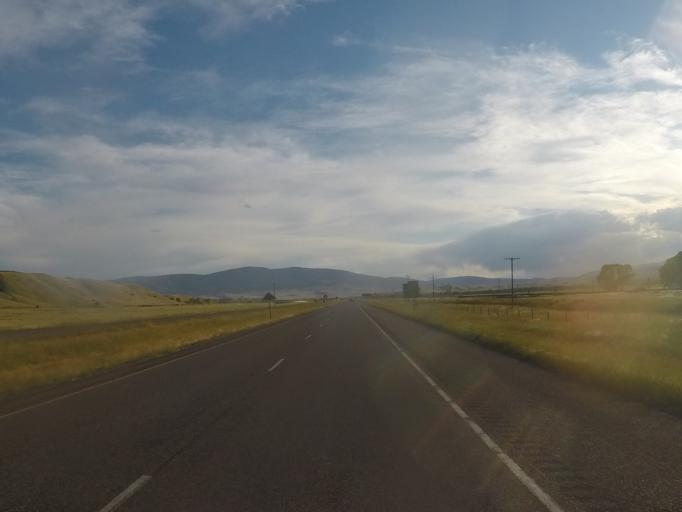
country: US
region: Montana
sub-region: Park County
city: Livingston
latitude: 45.6964
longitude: -110.4813
